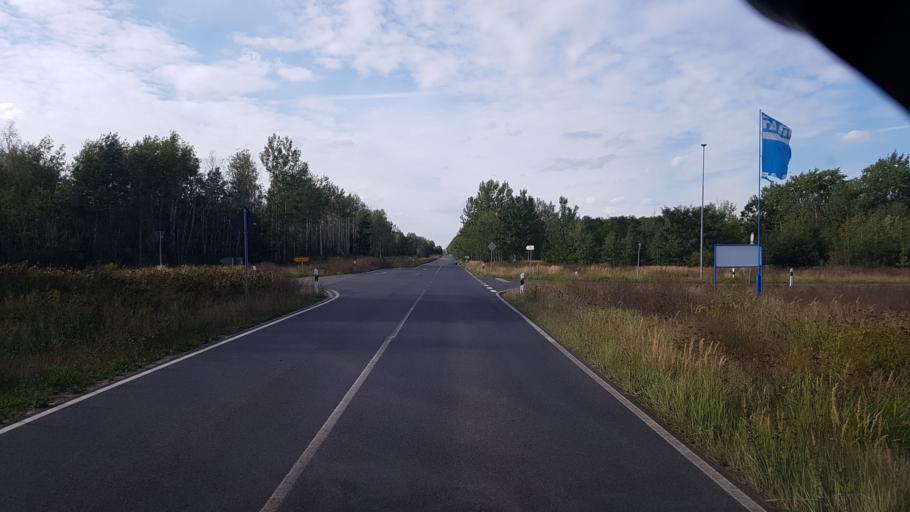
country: DE
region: Brandenburg
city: Welzow
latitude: 51.5407
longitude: 14.2339
